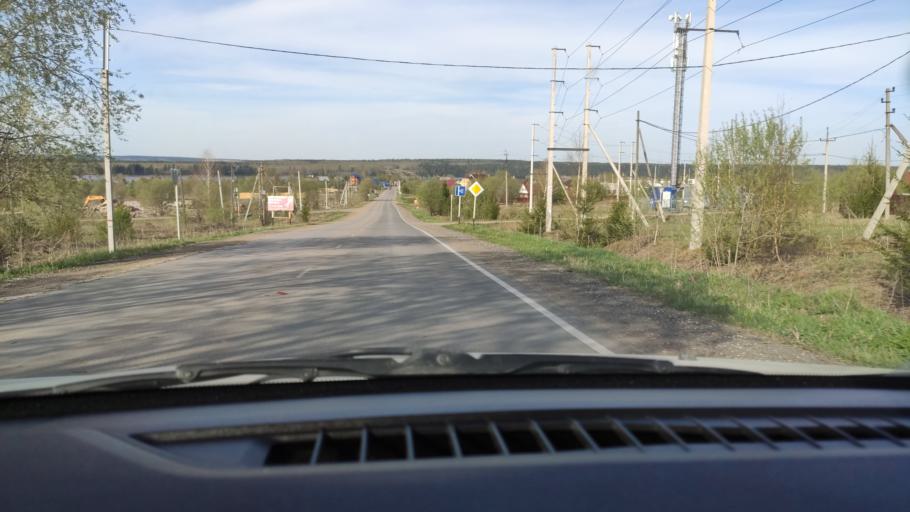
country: RU
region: Perm
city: Sylva
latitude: 57.9277
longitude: 56.6862
